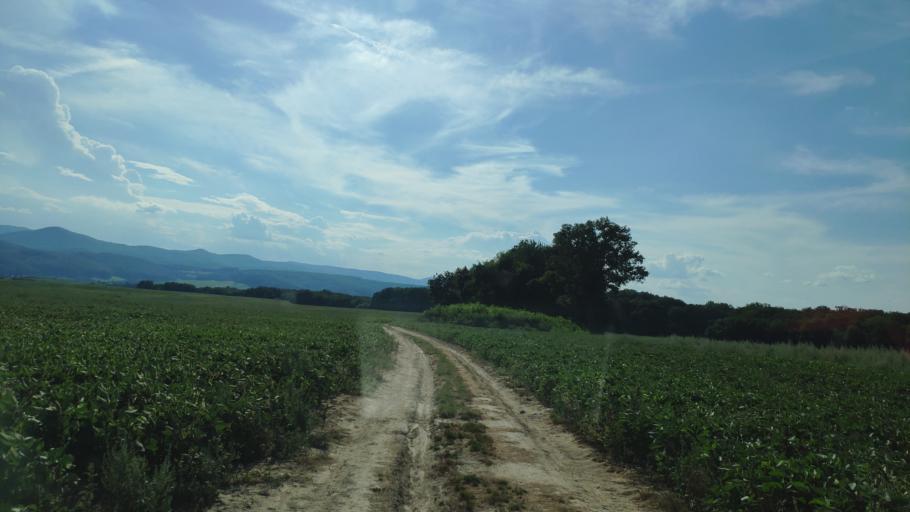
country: SK
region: Presovsky
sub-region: Okres Presov
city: Presov
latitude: 48.9170
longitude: 21.2940
